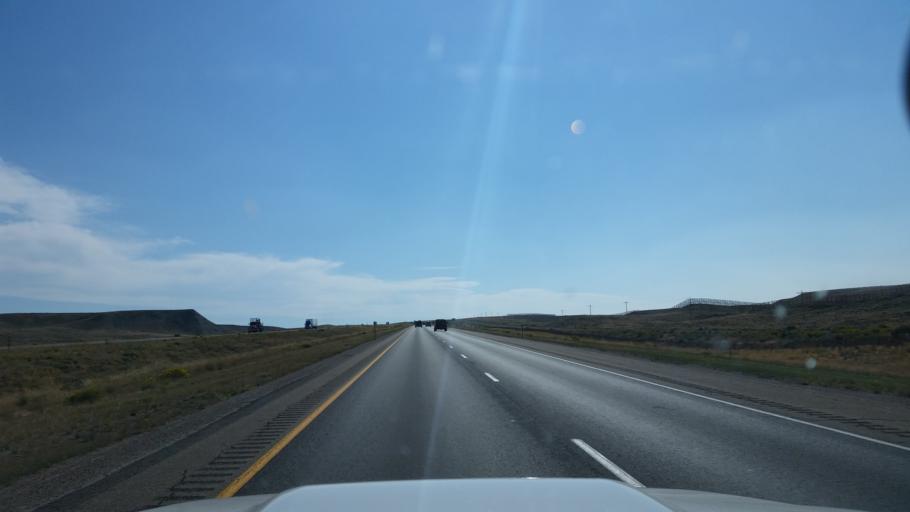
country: US
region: Wyoming
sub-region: Uinta County
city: Lyman
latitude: 41.5049
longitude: -109.9955
